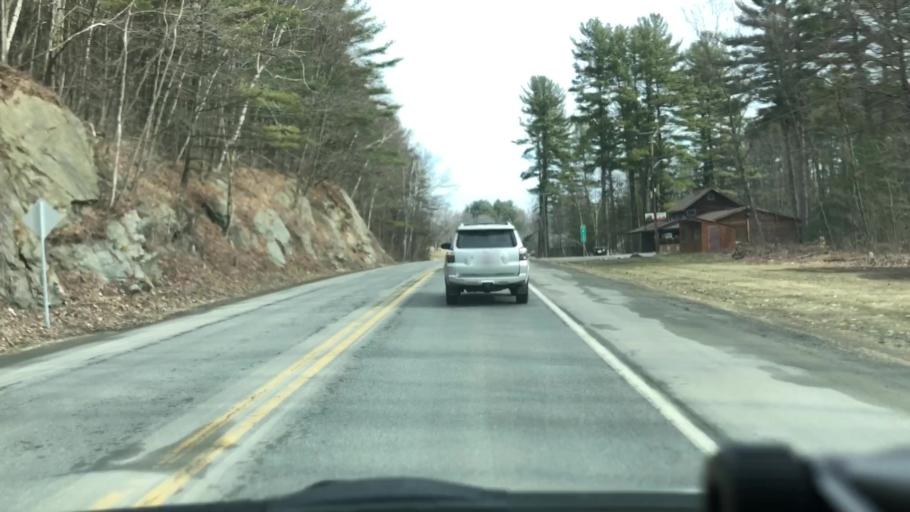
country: US
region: Massachusetts
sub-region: Franklin County
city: Shelburne
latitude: 42.6061
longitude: -72.6725
